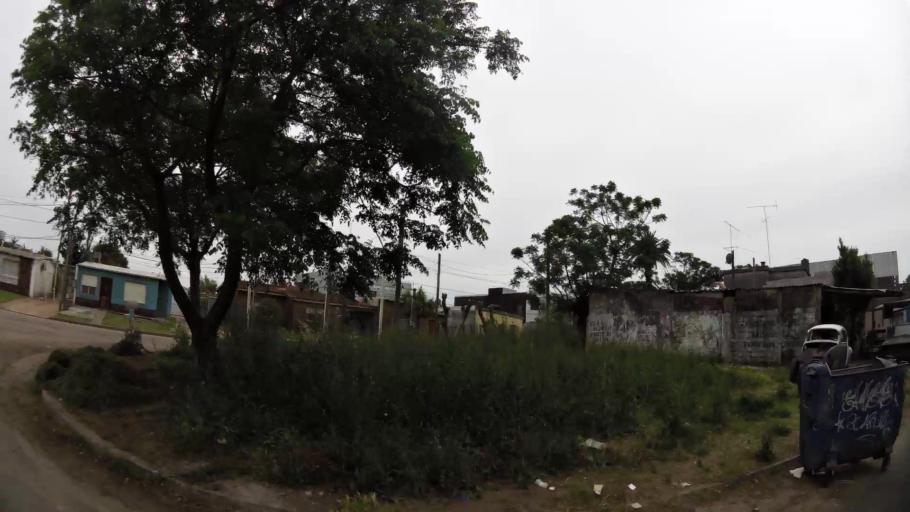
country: UY
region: Canelones
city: Las Piedras
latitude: -34.7319
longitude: -56.2145
